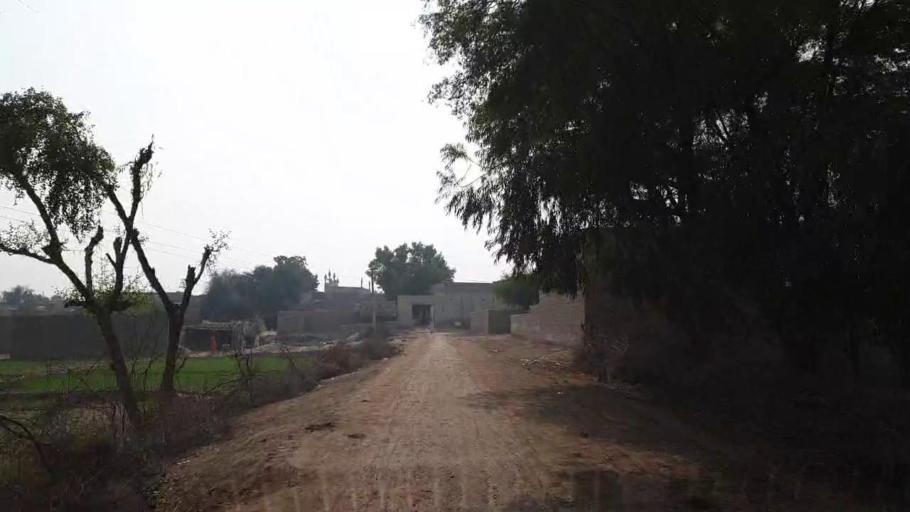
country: PK
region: Sindh
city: Bhan
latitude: 26.5175
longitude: 67.7349
